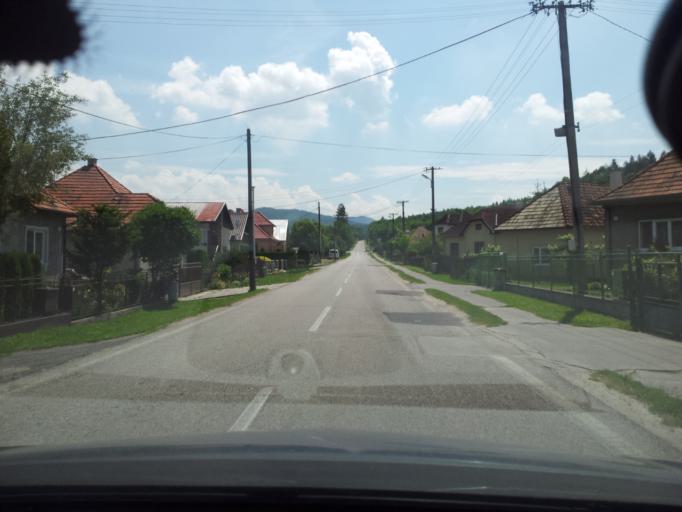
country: SK
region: Nitriansky
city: Partizanske
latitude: 48.6029
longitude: 18.4434
